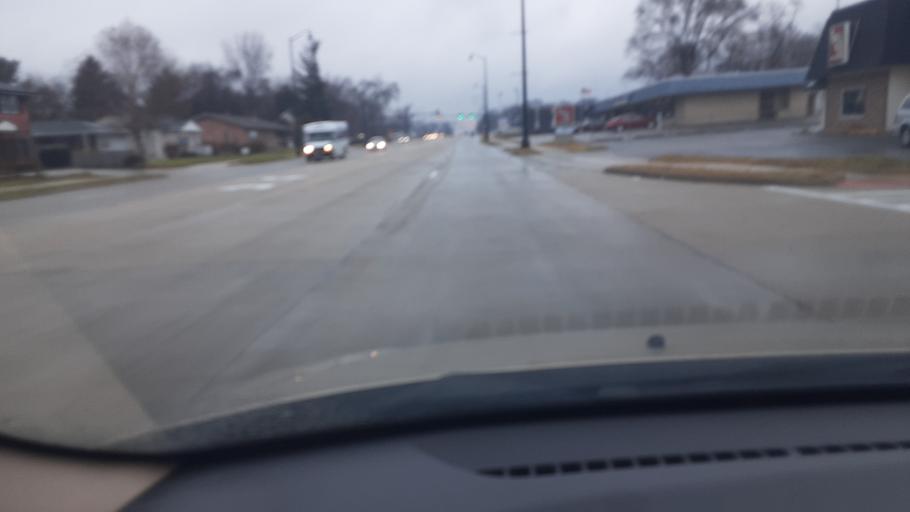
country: US
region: Illinois
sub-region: Winnebago County
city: Loves Park
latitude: 42.3121
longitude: -89.0771
